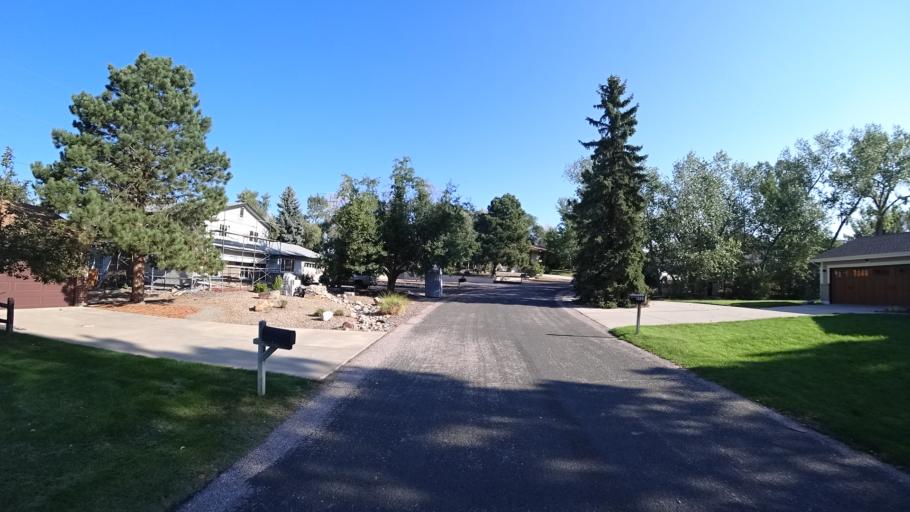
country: US
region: Colorado
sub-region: El Paso County
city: Air Force Academy
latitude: 38.9320
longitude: -104.7839
